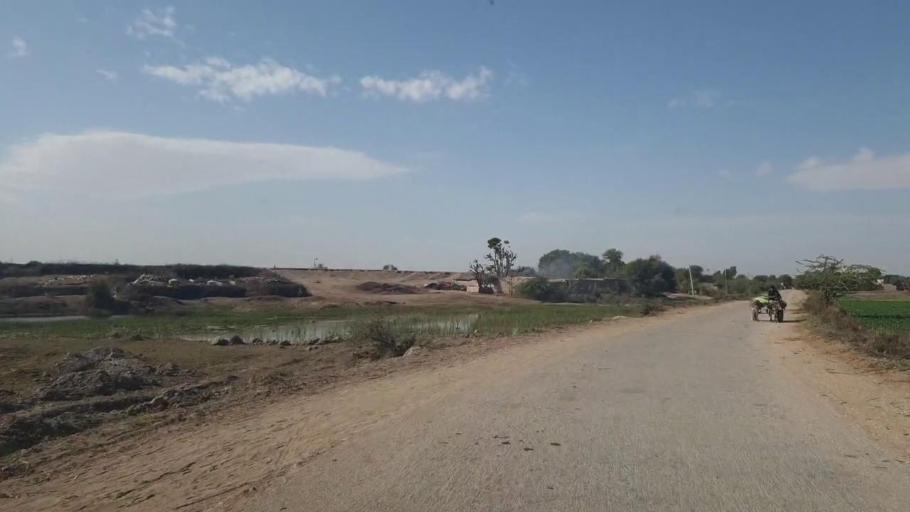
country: PK
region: Sindh
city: Hala
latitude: 25.9733
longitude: 68.3499
